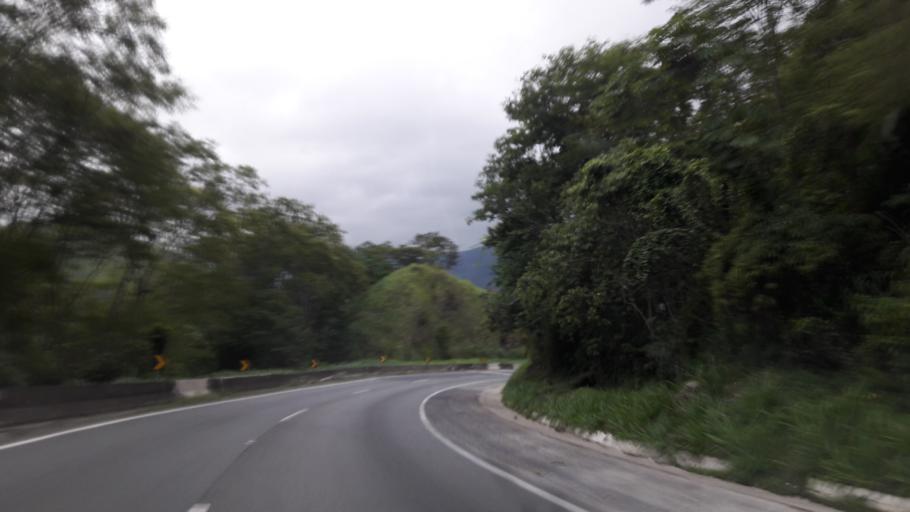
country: BR
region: Sao Paulo
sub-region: Cajati
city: Cajati
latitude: -24.8490
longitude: -48.2134
